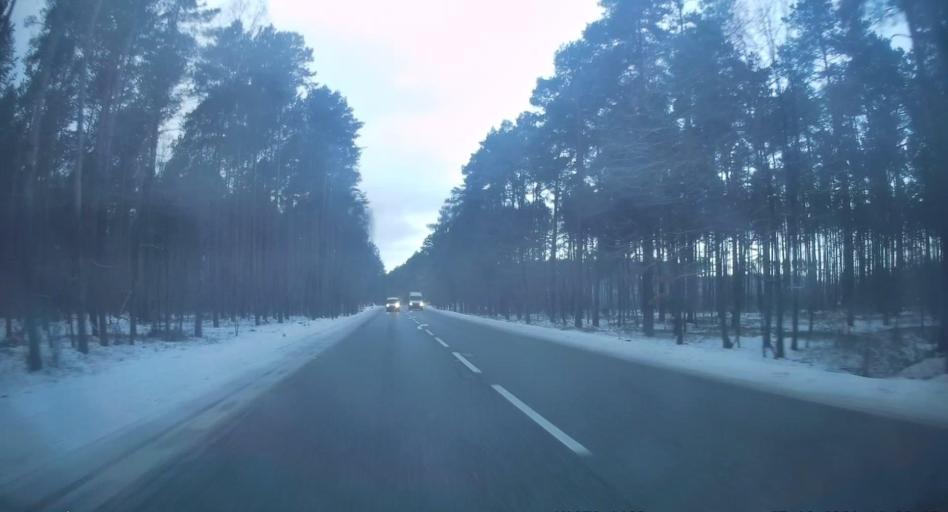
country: PL
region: Swietokrzyskie
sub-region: Powiat konecki
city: Smykow
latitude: 51.0953
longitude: 20.3434
